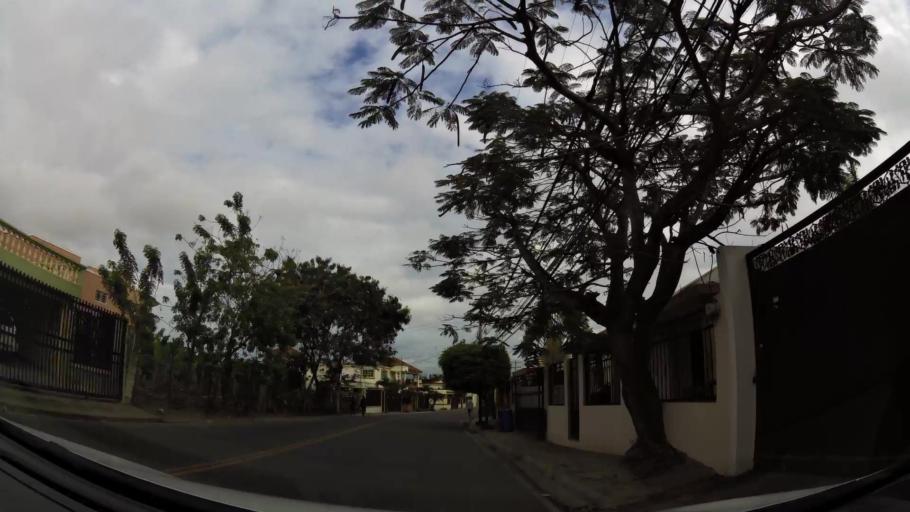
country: DO
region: Santiago
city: Santiago de los Caballeros
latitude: 19.4656
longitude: -70.6584
